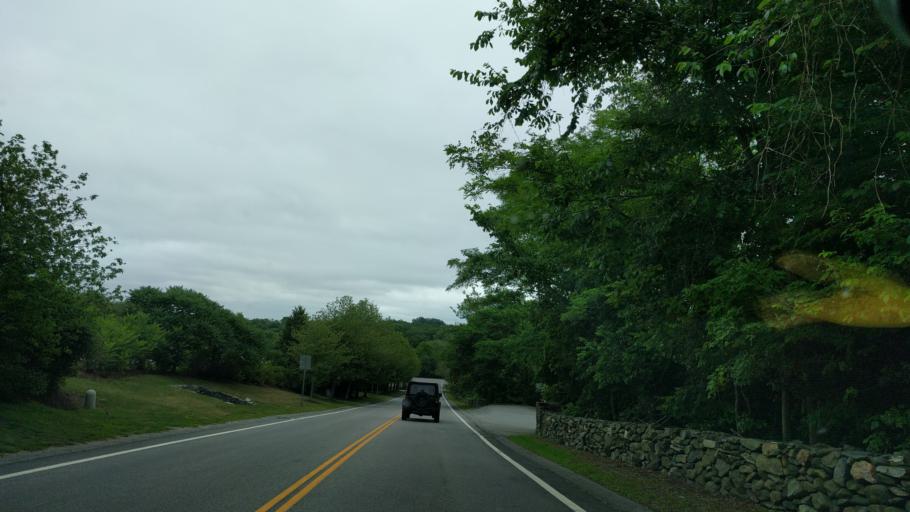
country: US
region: Rhode Island
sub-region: Newport County
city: Jamestown
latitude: 41.5258
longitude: -71.3779
